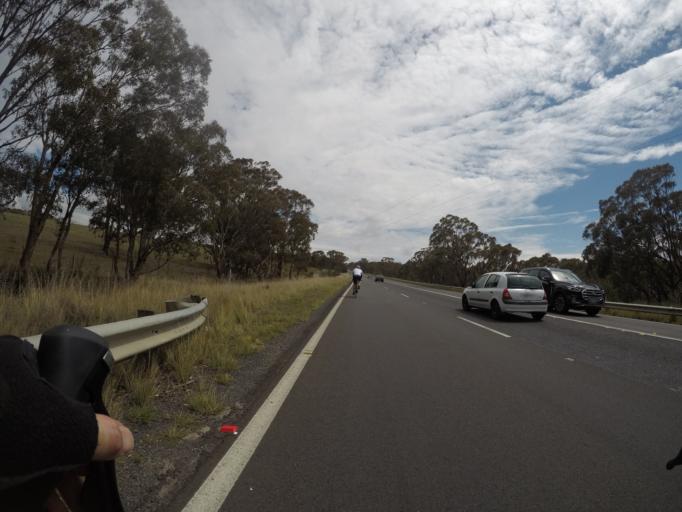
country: AU
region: New South Wales
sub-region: Bathurst Regional
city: Kelso
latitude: -33.4401
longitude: 149.7570
